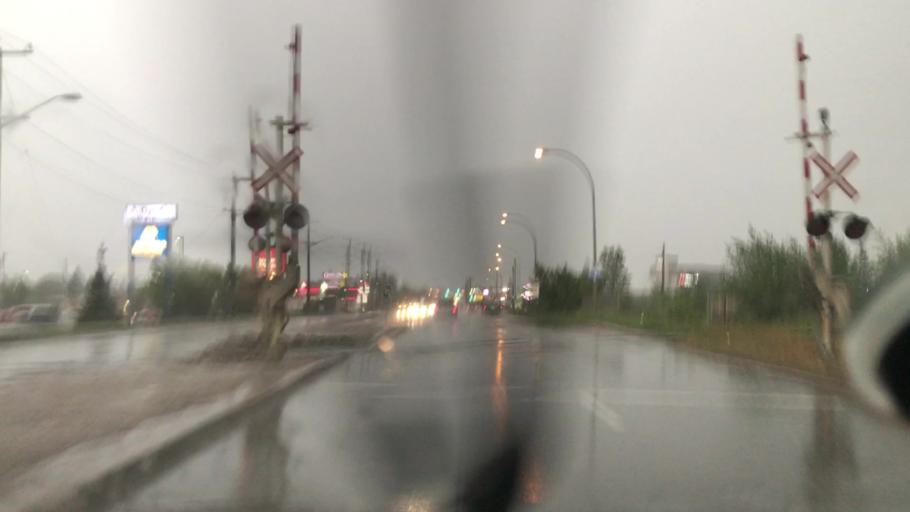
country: CA
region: Alberta
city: Edmonton
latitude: 53.5057
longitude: -113.4427
